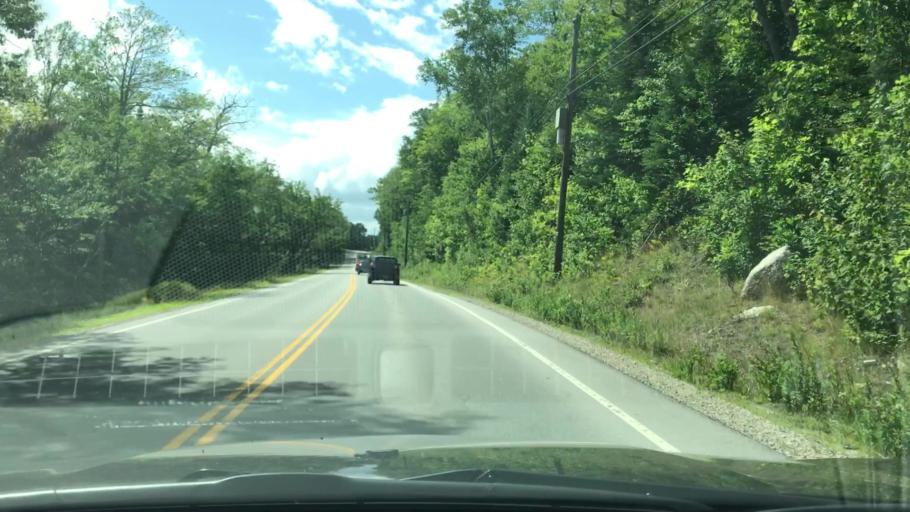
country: US
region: New Hampshire
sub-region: Coos County
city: Jefferson
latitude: 44.3618
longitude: -71.3798
